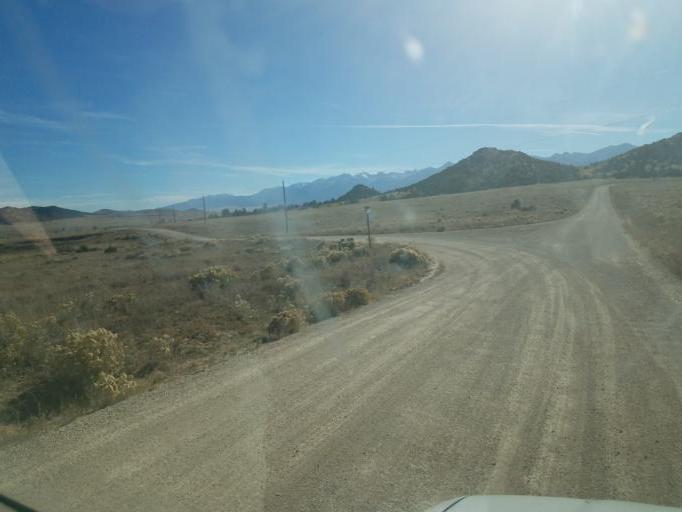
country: US
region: Colorado
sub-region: Custer County
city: Westcliffe
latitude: 38.2265
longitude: -105.4584
